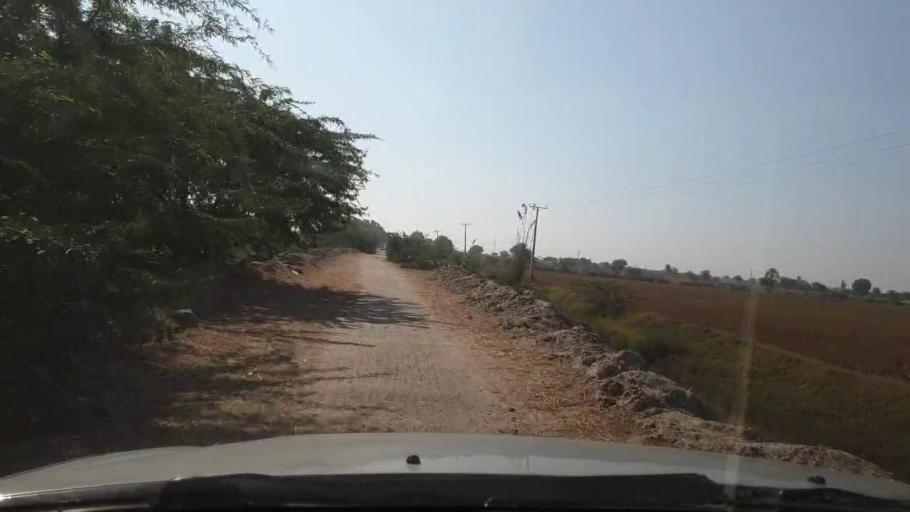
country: PK
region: Sindh
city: Kario
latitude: 24.8898
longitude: 68.5588
